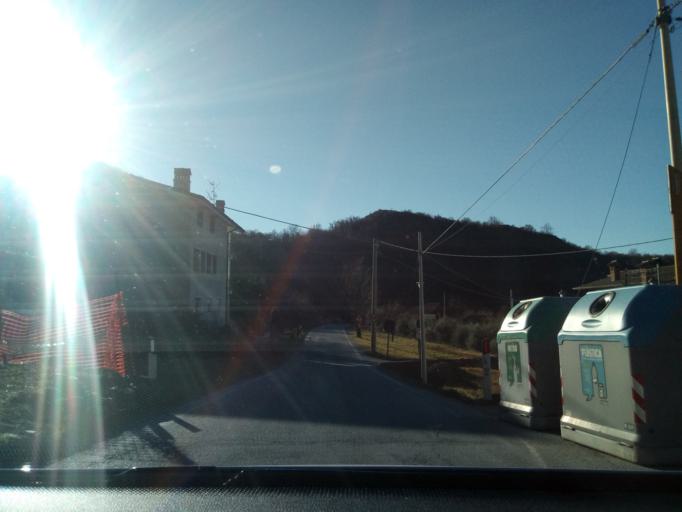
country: IT
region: Piedmont
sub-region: Provincia di Torino
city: Andrate
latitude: 45.5164
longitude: 7.8730
